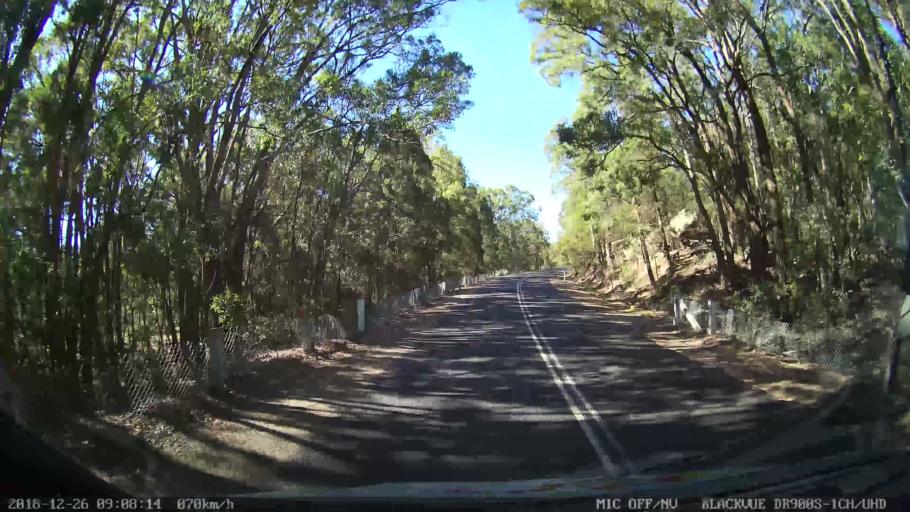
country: AU
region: New South Wales
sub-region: Mid-Western Regional
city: Kandos
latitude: -32.7145
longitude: 150.0032
